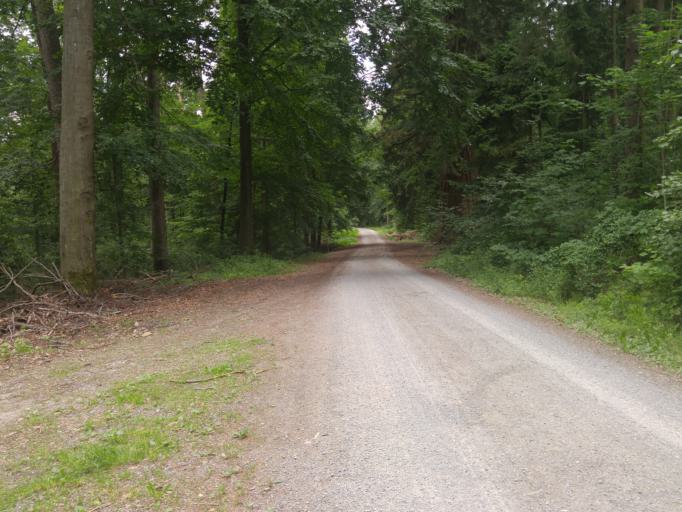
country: DE
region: Baden-Wuerttemberg
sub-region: Regierungsbezirk Stuttgart
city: Wustenrot
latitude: 49.0772
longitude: 9.4477
